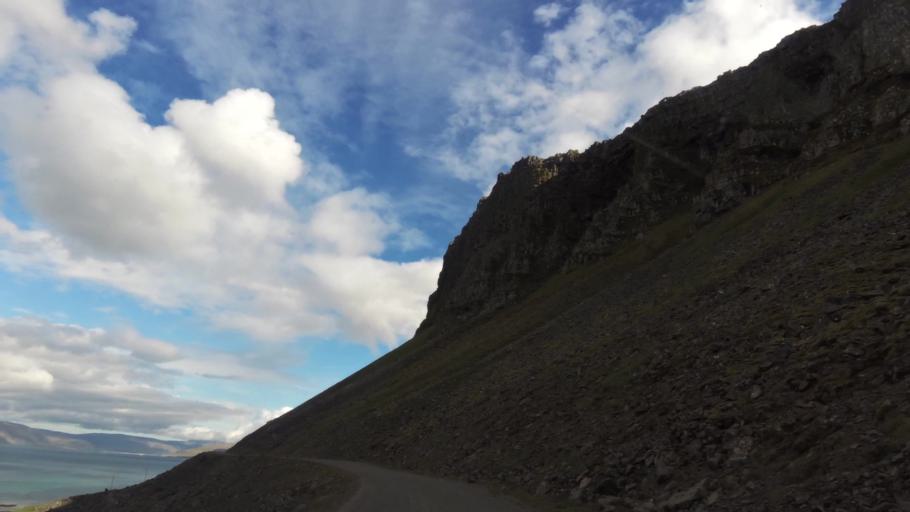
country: IS
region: West
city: Olafsvik
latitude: 65.6009
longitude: -24.1421
